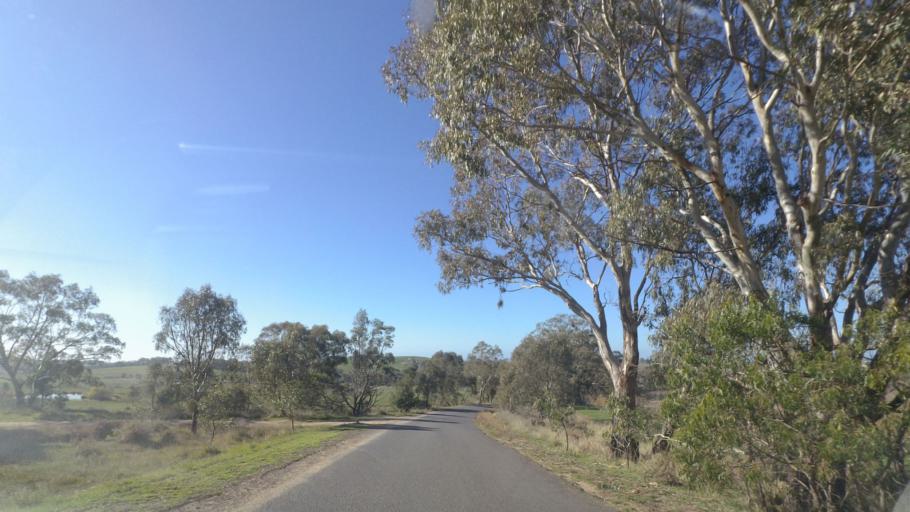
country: AU
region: Victoria
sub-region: Mount Alexander
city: Castlemaine
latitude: -36.9685
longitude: 144.3097
